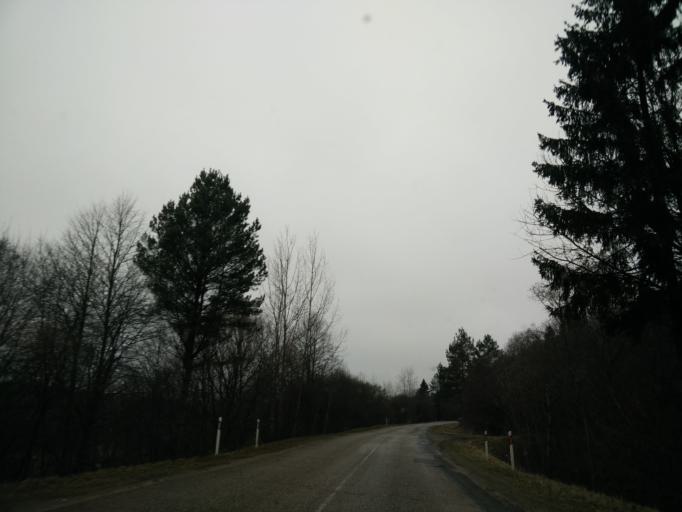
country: LT
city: Ariogala
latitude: 55.2876
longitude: 23.4445
